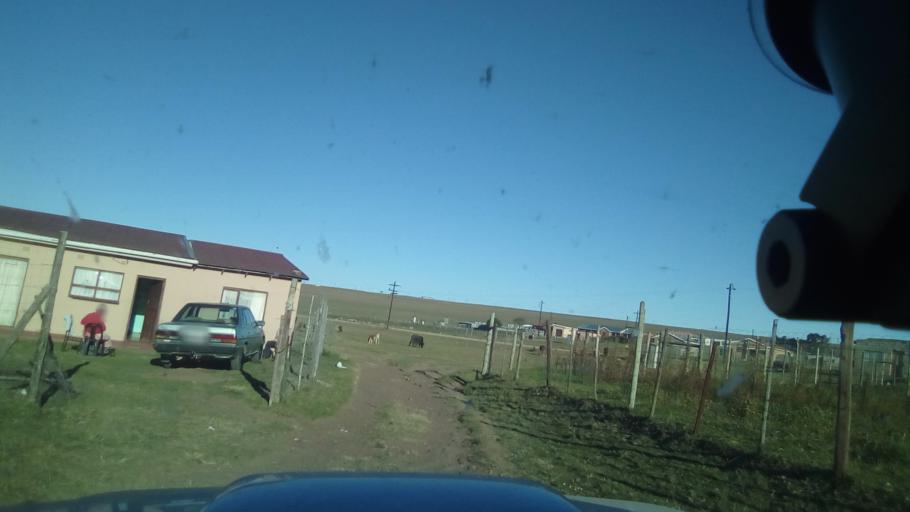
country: ZA
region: Eastern Cape
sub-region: Buffalo City Metropolitan Municipality
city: Bhisho
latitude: -32.9511
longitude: 27.2957
